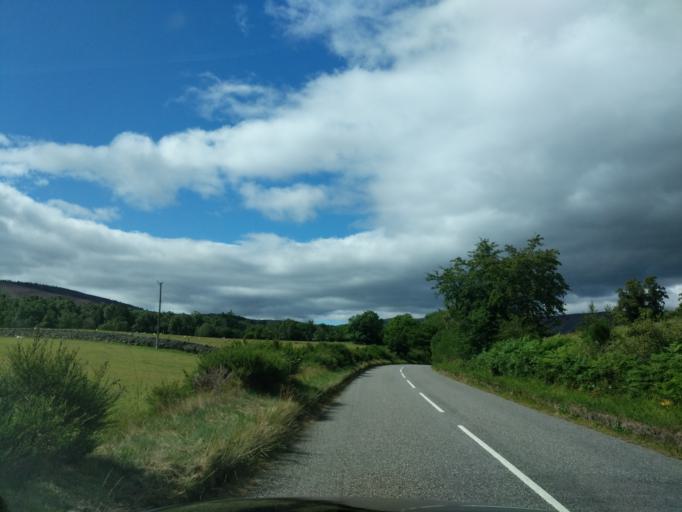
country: GB
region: Scotland
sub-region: Aberdeenshire
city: Ballater
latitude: 57.0567
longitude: -2.9341
